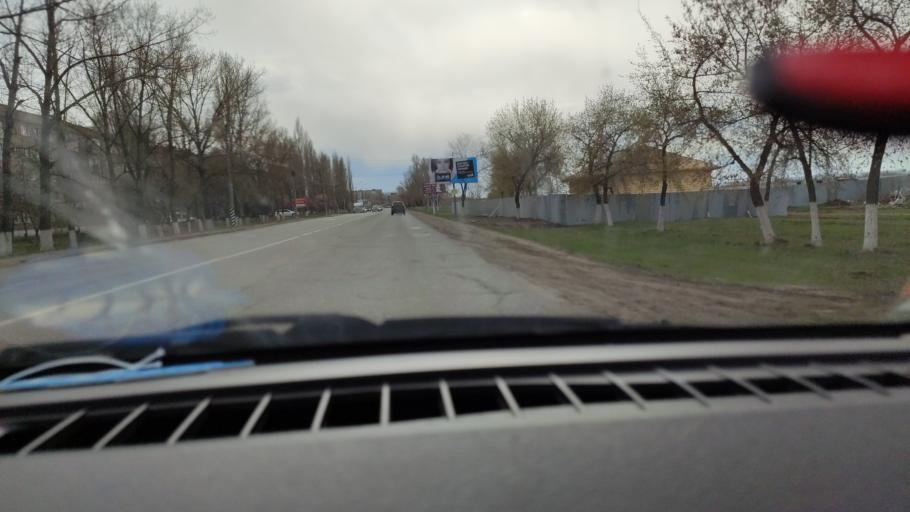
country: RU
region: Saratov
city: Engel's
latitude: 51.4534
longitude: 46.0846
